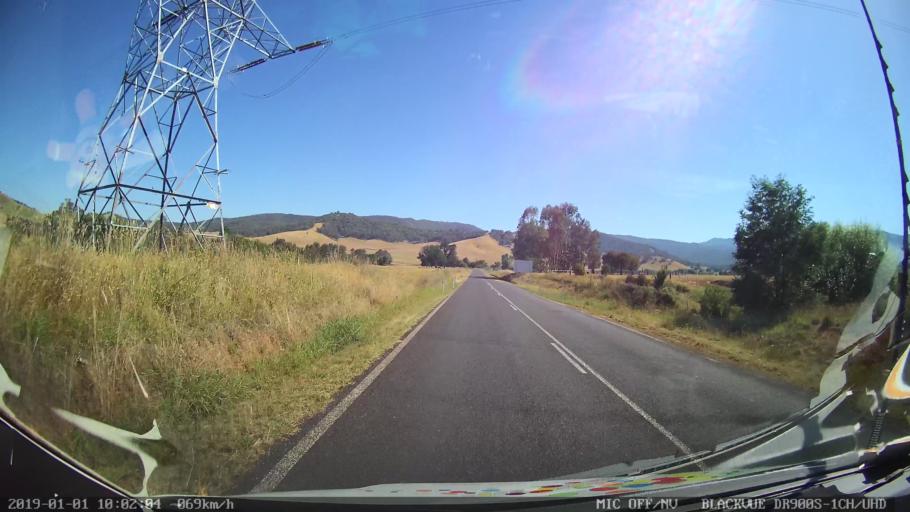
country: AU
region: New South Wales
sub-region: Snowy River
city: Jindabyne
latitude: -36.1850
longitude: 148.1014
